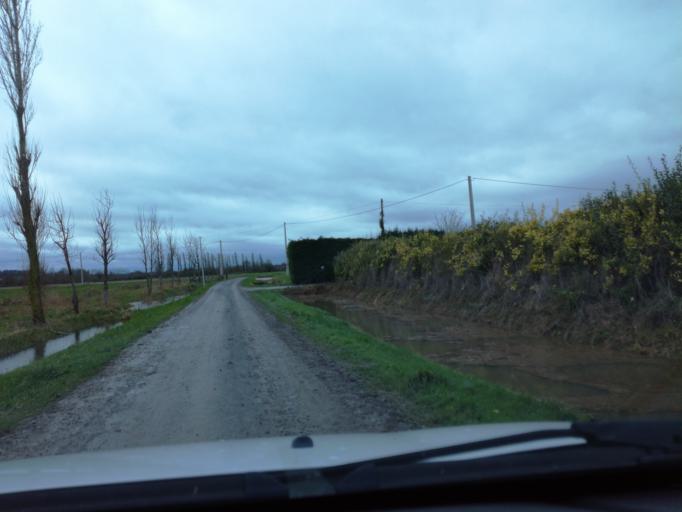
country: FR
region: Brittany
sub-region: Departement d'Ille-et-Vilaine
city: Baguer-Pican
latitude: 48.5792
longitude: -1.6948
